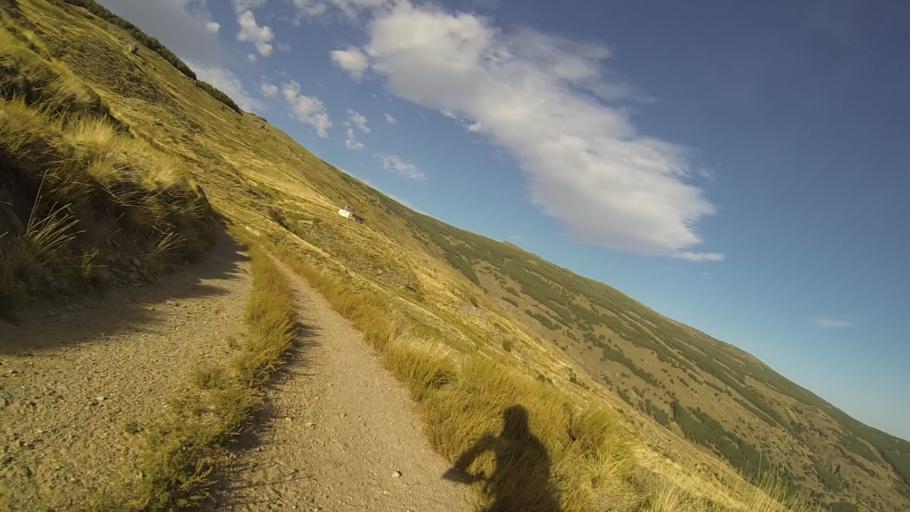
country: ES
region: Andalusia
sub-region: Provincia de Almeria
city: Laujar de Andarax
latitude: 37.0752
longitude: -2.8873
